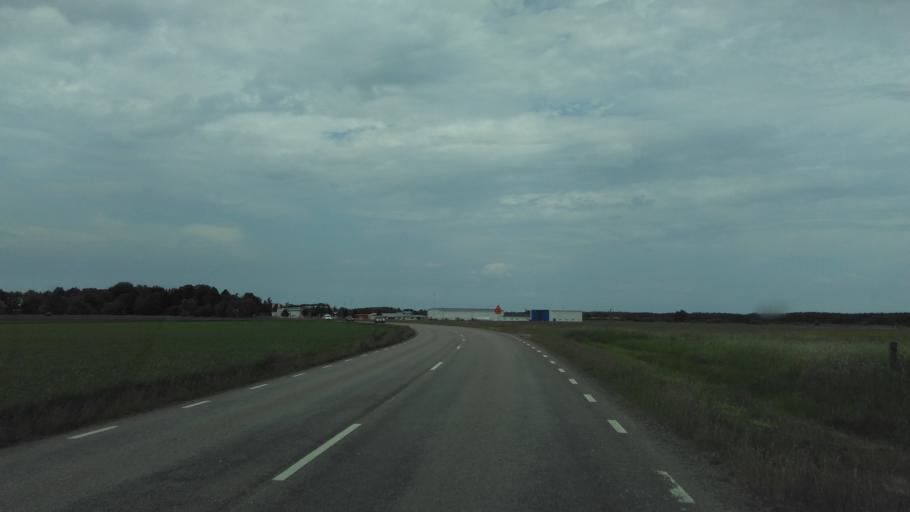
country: SE
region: Vaestra Goetaland
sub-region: Lidkopings Kommun
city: Lidkoping
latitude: 58.4569
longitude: 13.1566
